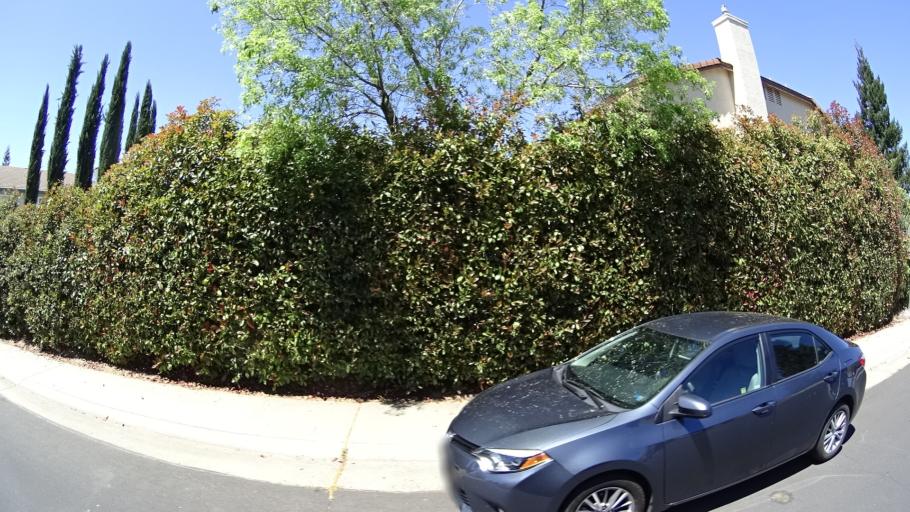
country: US
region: California
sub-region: Placer County
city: Rocklin
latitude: 38.8202
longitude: -121.2663
